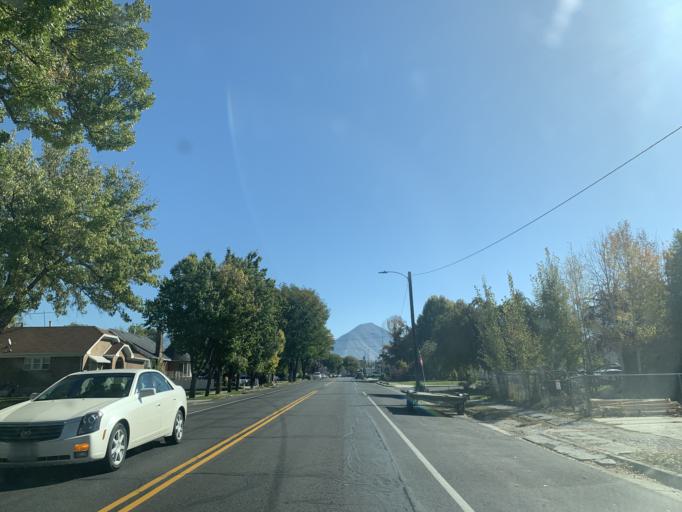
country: US
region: Utah
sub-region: Utah County
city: Payson
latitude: 40.0436
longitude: -111.7366
